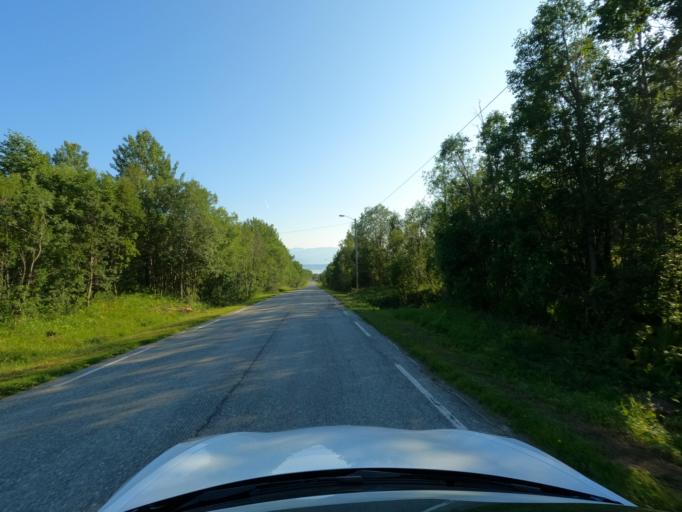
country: NO
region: Nordland
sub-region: Narvik
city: Bjerkvik
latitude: 68.5394
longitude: 17.4885
